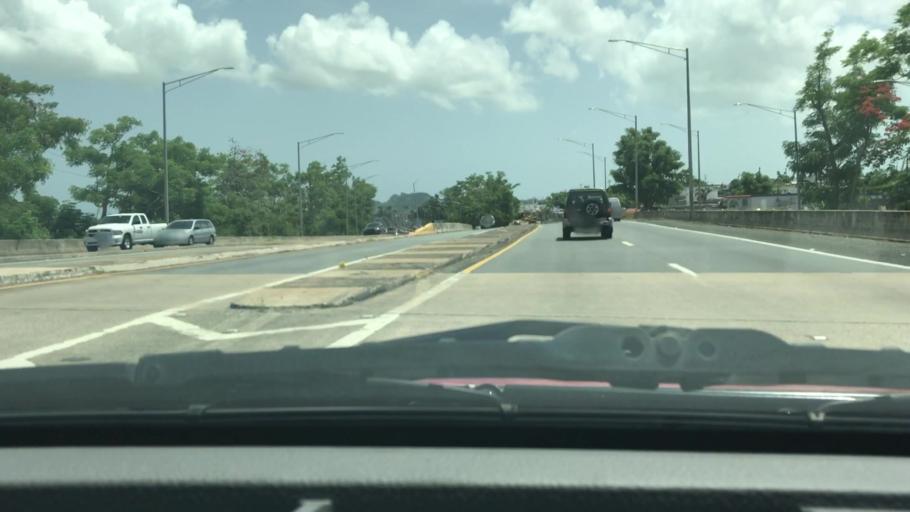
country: PR
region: Bayamon
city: Bayamon
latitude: 18.3733
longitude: -66.1644
